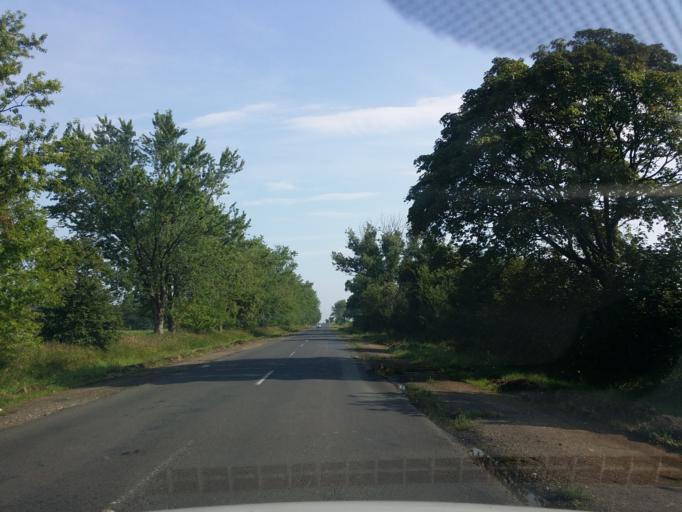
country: HU
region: Borsod-Abauj-Zemplen
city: Abaujszanto
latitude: 48.3594
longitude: 21.2155
